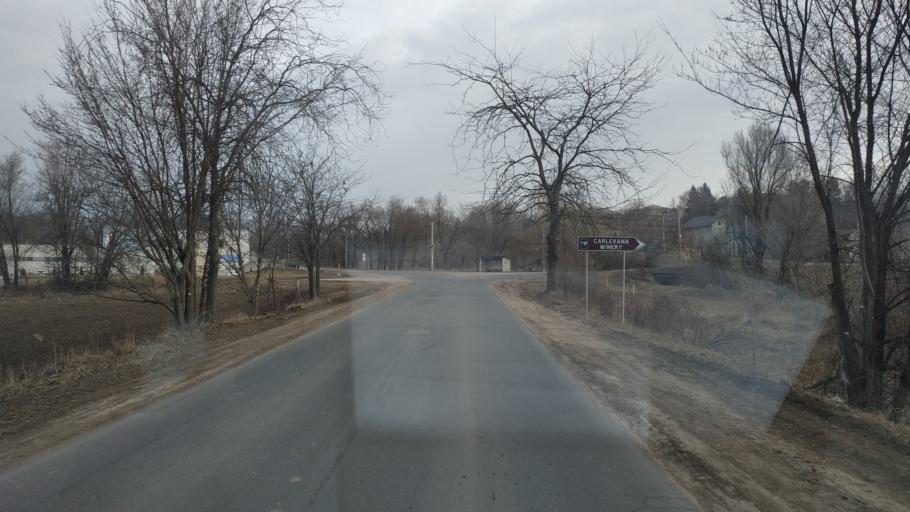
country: MD
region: Chisinau
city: Singera
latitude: 46.9261
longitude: 29.0485
